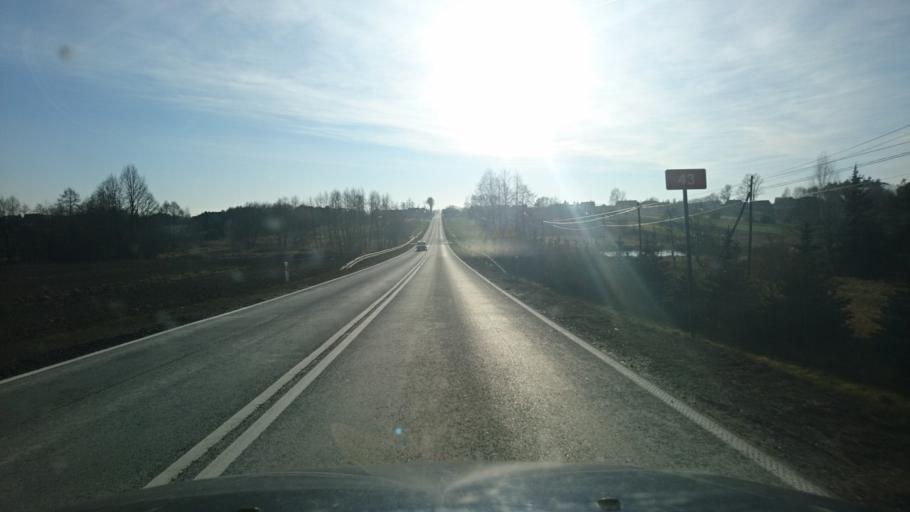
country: PL
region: Opole Voivodeship
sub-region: Powiat oleski
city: Dalachow
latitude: 51.0564
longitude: 18.5990
